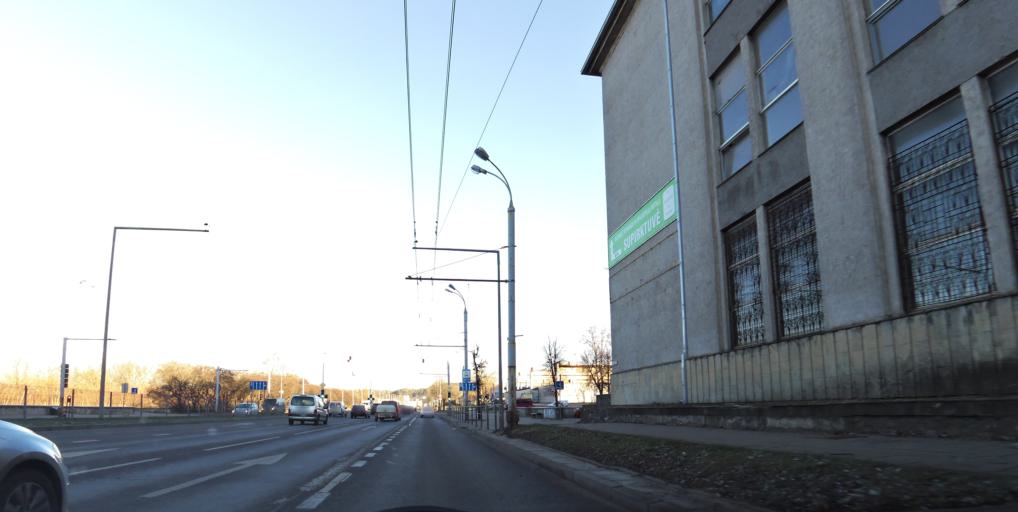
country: LT
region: Vilnius County
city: Lazdynai
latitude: 54.6536
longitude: 25.2234
